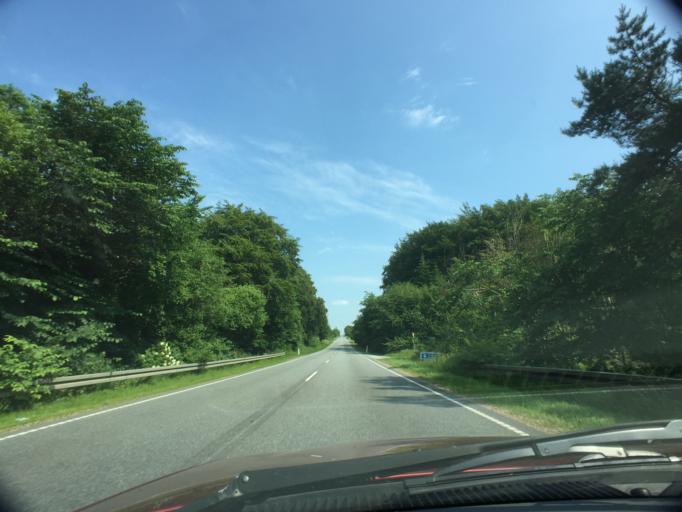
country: DK
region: Central Jutland
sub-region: Favrskov Kommune
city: Hammel
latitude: 56.2444
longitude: 9.7849
